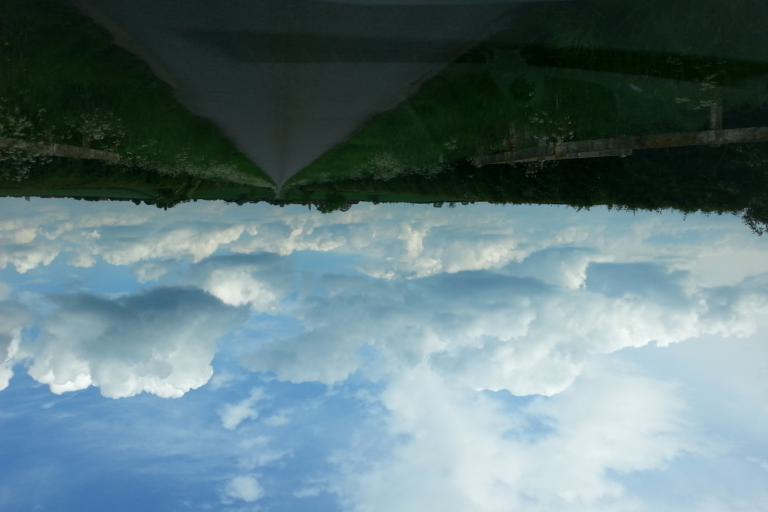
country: GB
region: England
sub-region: Lincolnshire
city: Long Bennington
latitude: 53.0009
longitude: -0.7339
